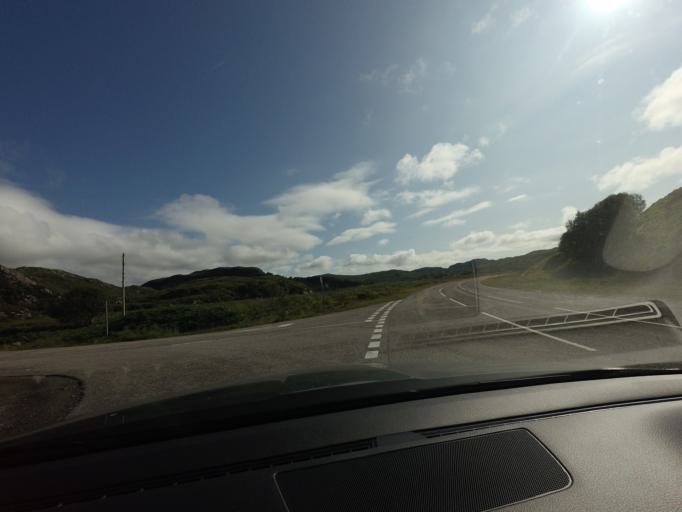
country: GB
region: Scotland
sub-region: Highland
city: Ullapool
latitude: 58.3739
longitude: -5.0169
